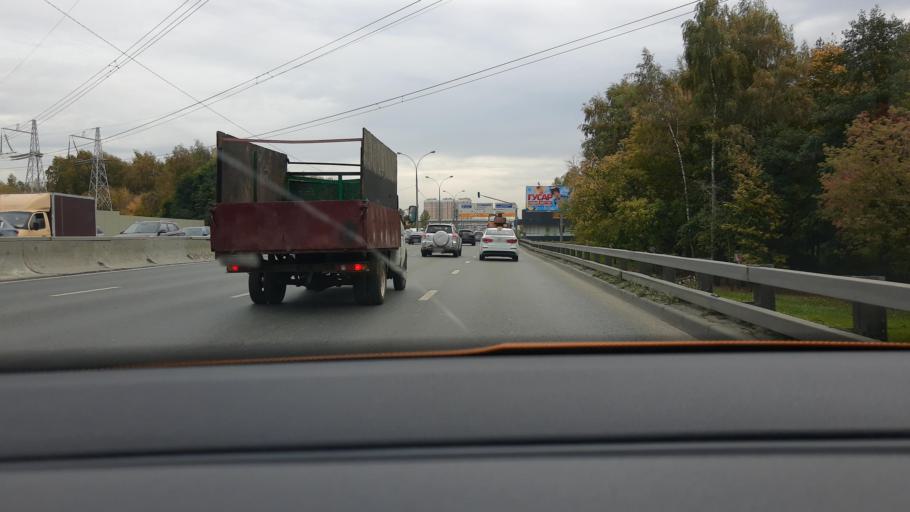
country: RU
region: Moscow
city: Vykhino-Zhulebino
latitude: 55.6909
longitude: 37.8191
